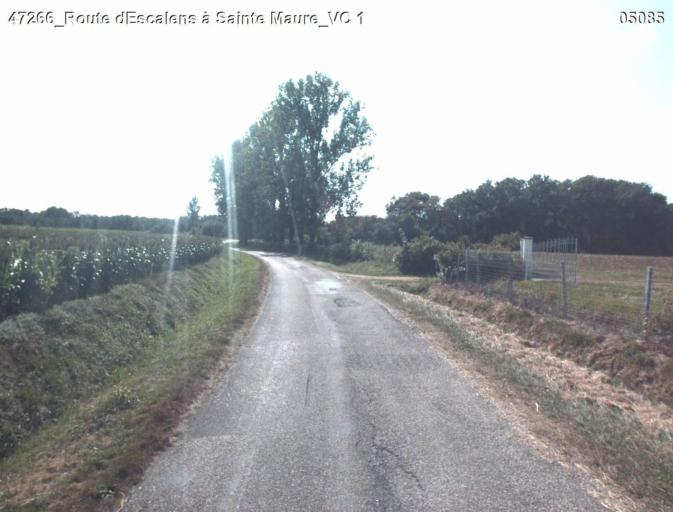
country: FR
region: Midi-Pyrenees
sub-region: Departement du Gers
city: Montreal
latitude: 44.0127
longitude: 0.1173
